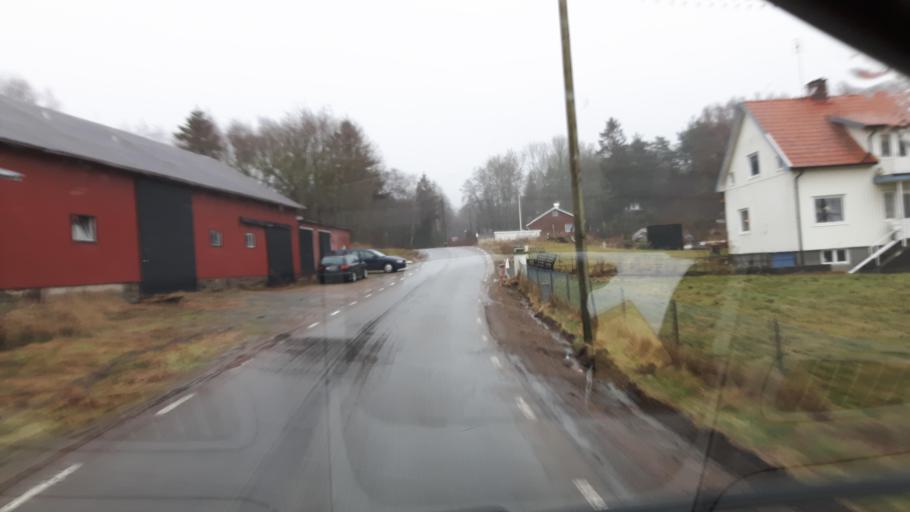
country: SE
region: Halland
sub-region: Kungsbacka Kommun
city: Frillesas
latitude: 57.3648
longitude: 12.1427
